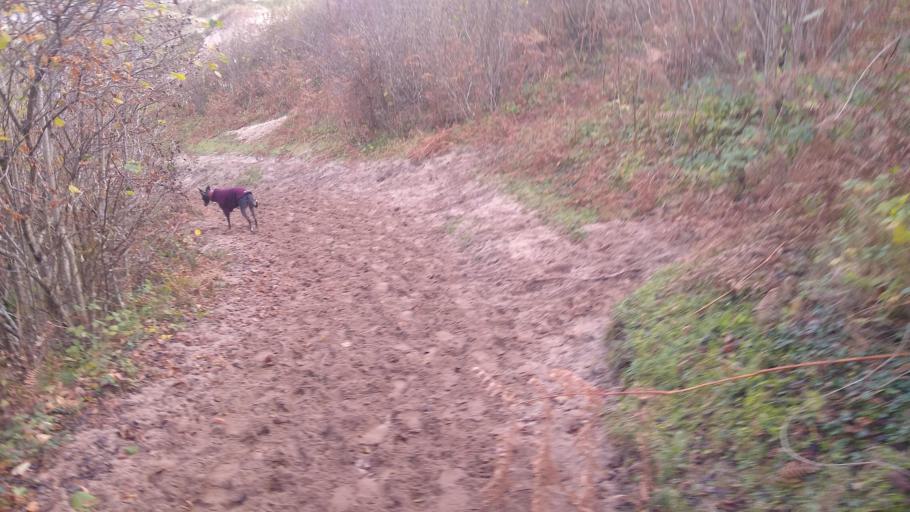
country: GB
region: Wales
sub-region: City and County of Swansea
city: Southgate
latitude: 51.5729
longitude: -4.1163
